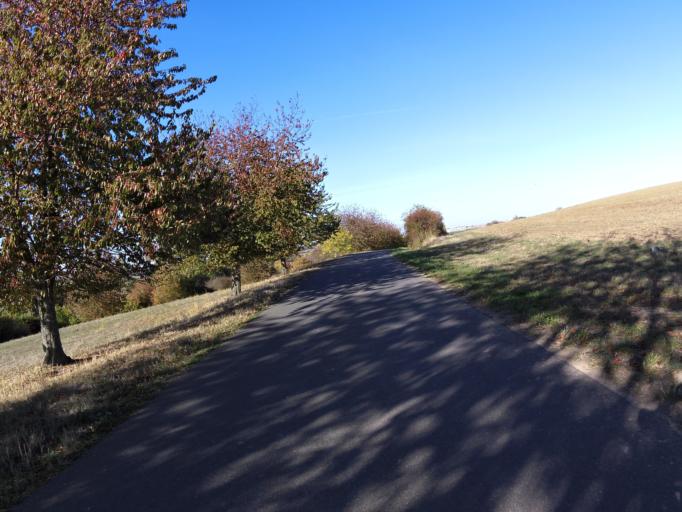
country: DE
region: Bavaria
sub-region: Regierungsbezirk Unterfranken
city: Geroldshausen
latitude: 49.6994
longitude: 9.9307
